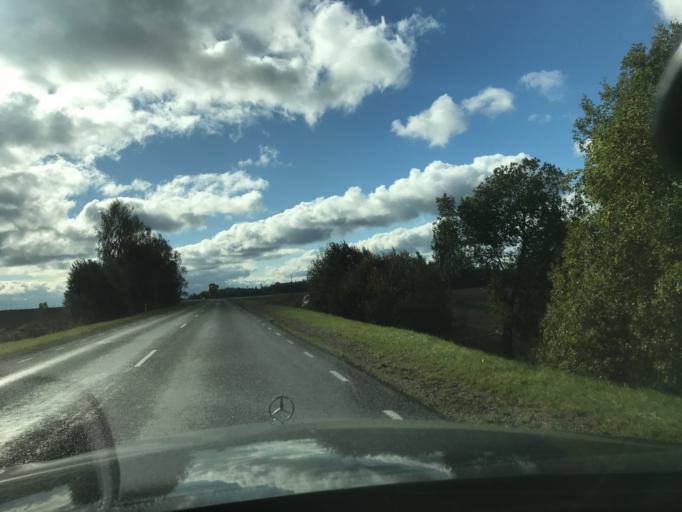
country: EE
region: Tartu
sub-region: Elva linn
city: Elva
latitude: 57.9779
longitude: 26.2608
